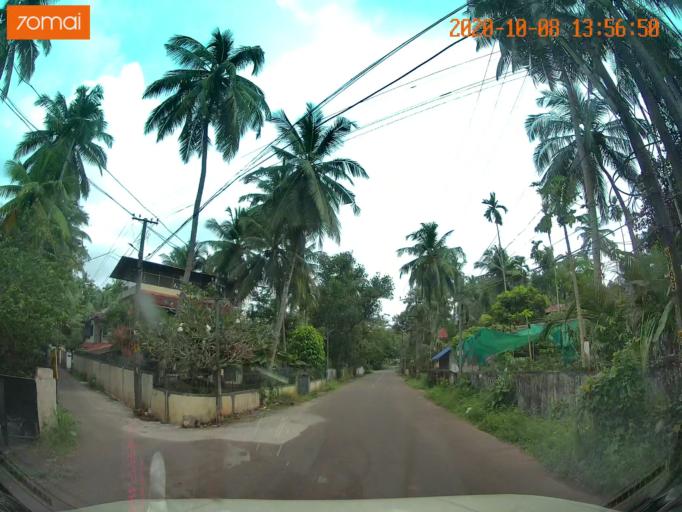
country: IN
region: Kerala
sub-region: Kozhikode
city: Kozhikode
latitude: 11.2915
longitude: 75.8005
